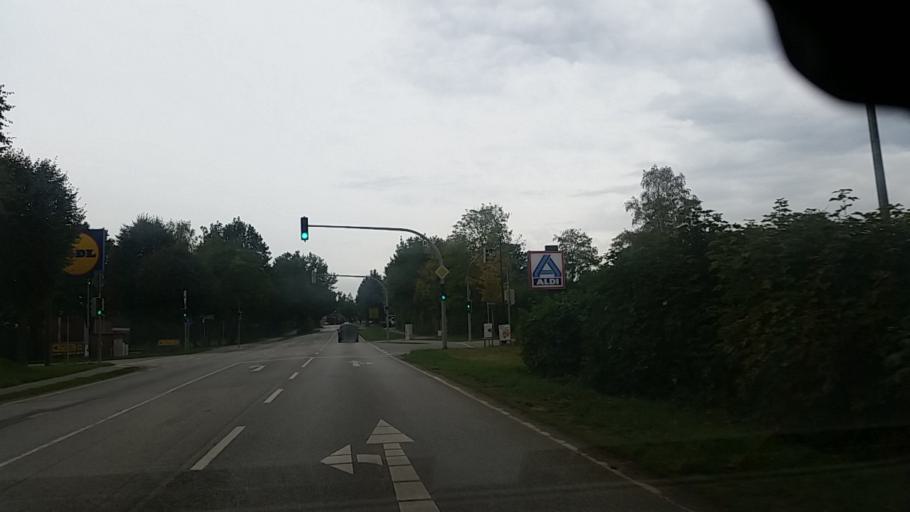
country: DE
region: Schleswig-Holstein
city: Nahe
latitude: 53.7995
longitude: 10.1459
